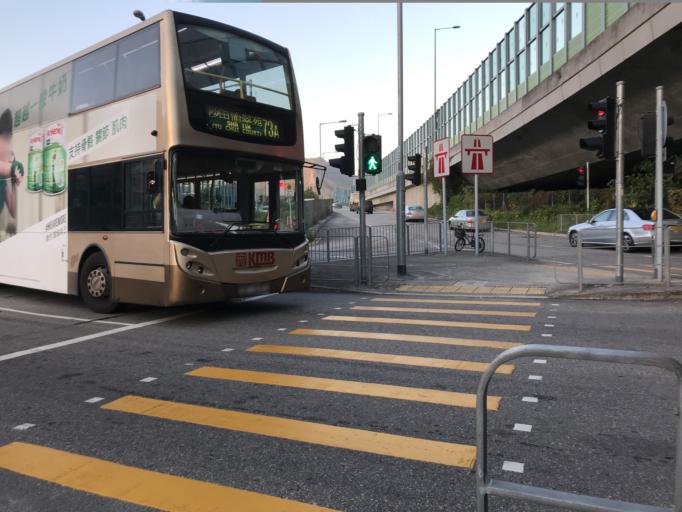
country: HK
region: Tai Po
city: Tai Po
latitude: 22.4629
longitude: 114.1484
